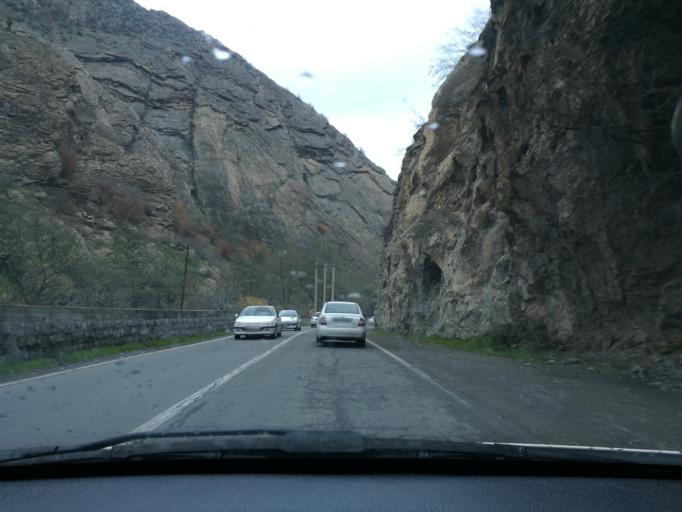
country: IR
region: Mazandaran
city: Chalus
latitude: 36.3186
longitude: 51.2500
